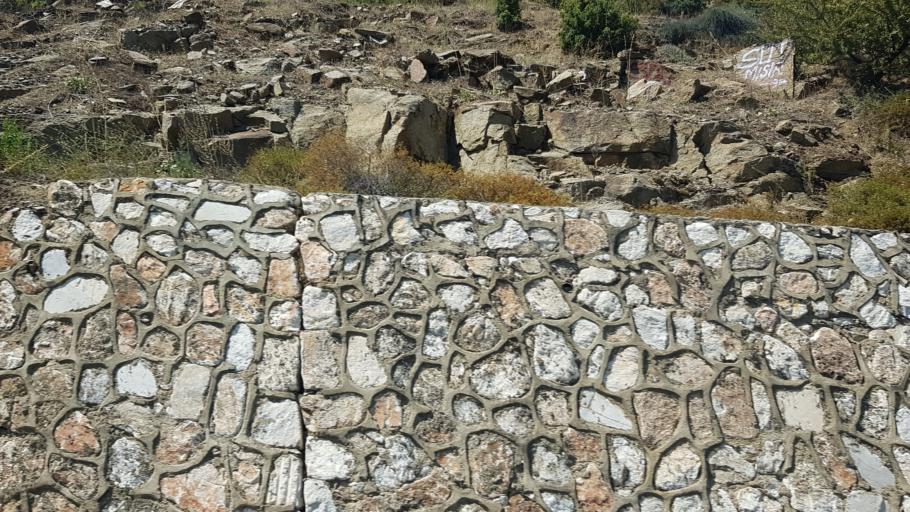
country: TR
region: Aydin
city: Akcaova
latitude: 37.5077
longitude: 28.1020
